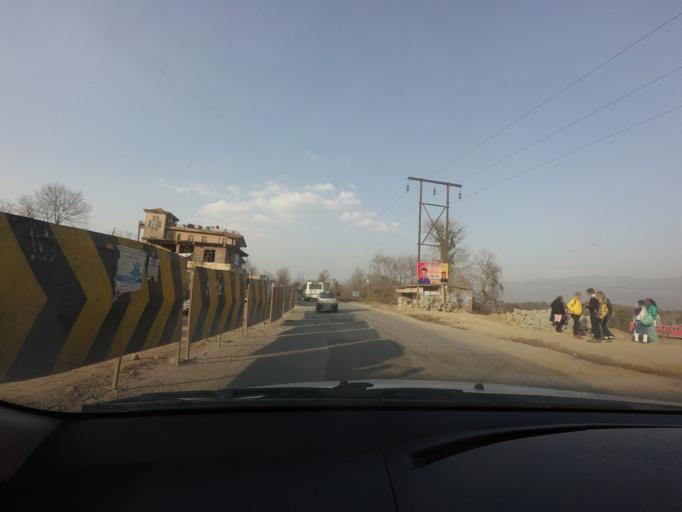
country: IN
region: Himachal Pradesh
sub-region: Mandi
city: Sundarnagar
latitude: 31.5687
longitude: 76.9069
